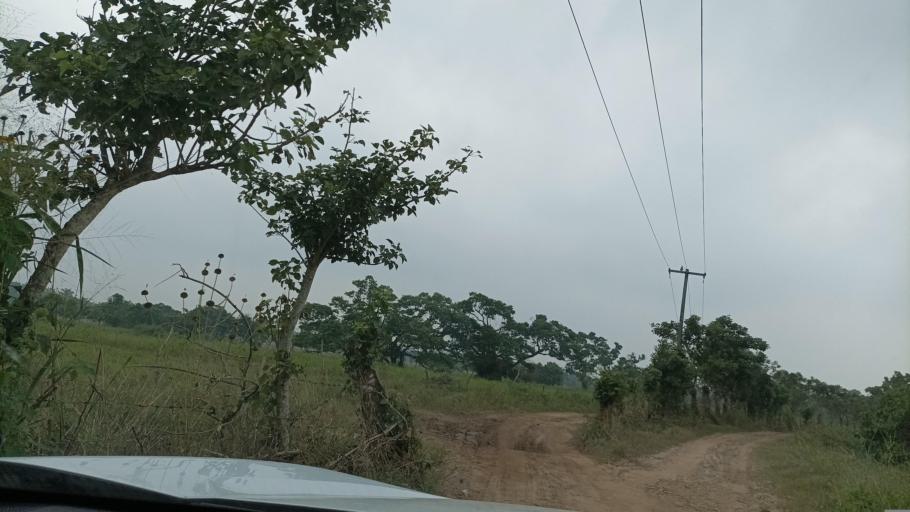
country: MX
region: Veracruz
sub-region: Uxpanapa
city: Poblado 10
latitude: 17.5582
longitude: -94.2263
